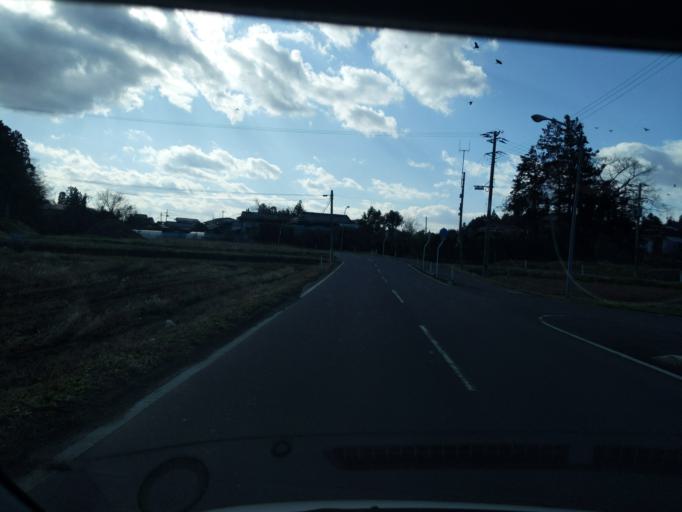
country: JP
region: Iwate
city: Ichinoseki
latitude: 38.7612
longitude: 141.0589
